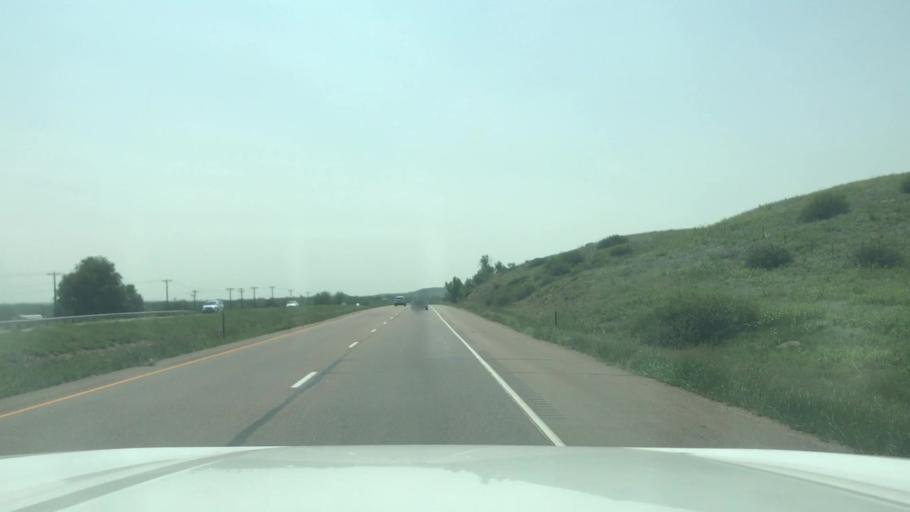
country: US
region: Colorado
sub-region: El Paso County
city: Fountain
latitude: 38.6918
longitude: -104.7196
